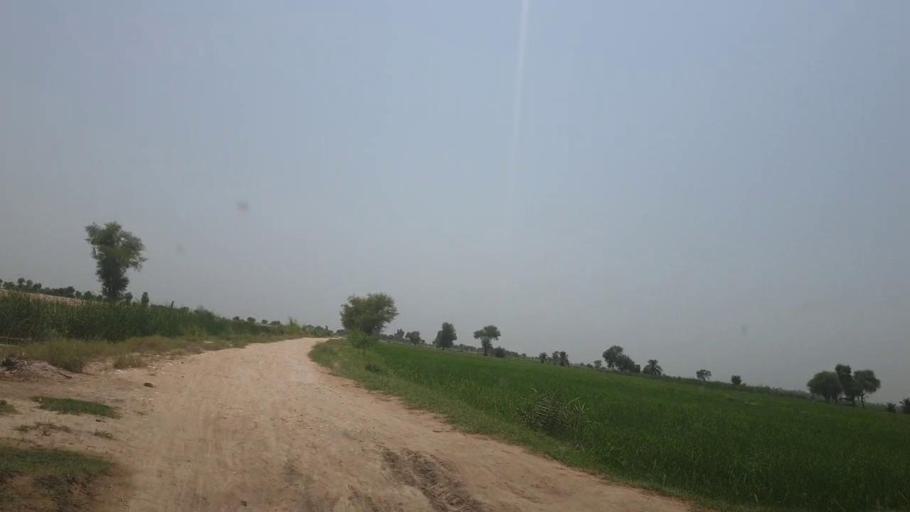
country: PK
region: Sindh
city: Lakhi
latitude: 27.8578
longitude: 68.6647
